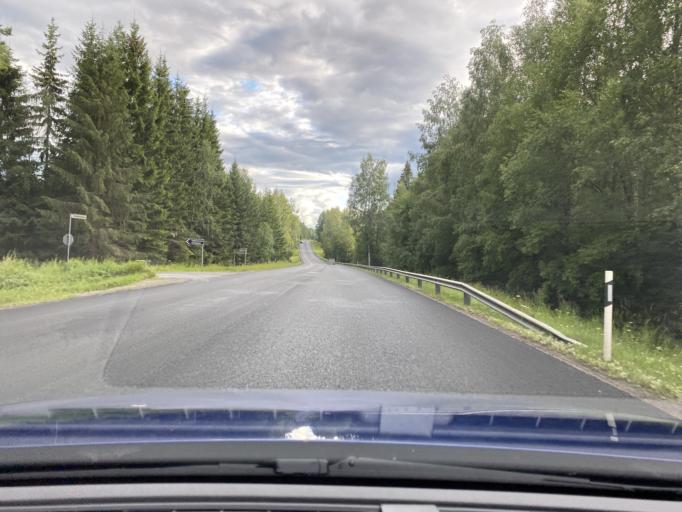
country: FI
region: Haeme
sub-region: Haemeenlinna
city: Haemeenlinna
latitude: 60.9531
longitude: 24.4082
